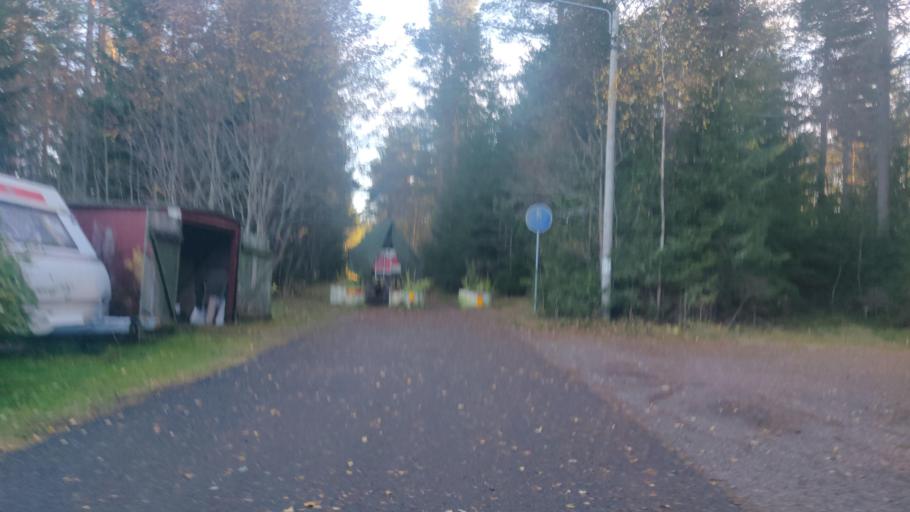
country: SE
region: Vaesternorrland
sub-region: Sundsvalls Kommun
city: Njurundabommen
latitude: 62.2704
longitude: 17.3973
